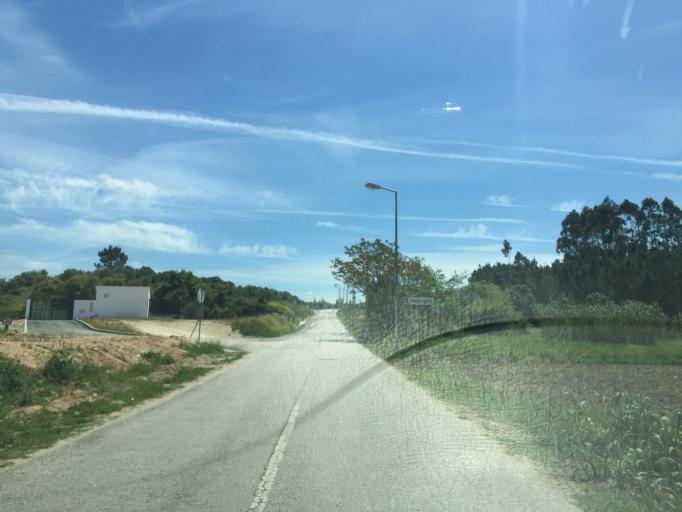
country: PT
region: Leiria
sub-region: Pombal
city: Lourical
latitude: 40.0685
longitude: -8.7306
